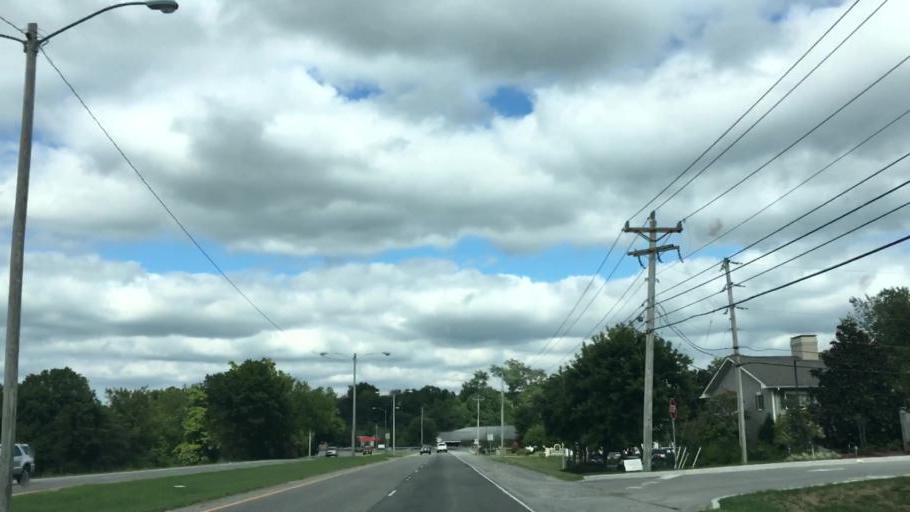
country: US
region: Tennessee
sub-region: Maury County
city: Columbia
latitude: 35.6140
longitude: -87.0666
